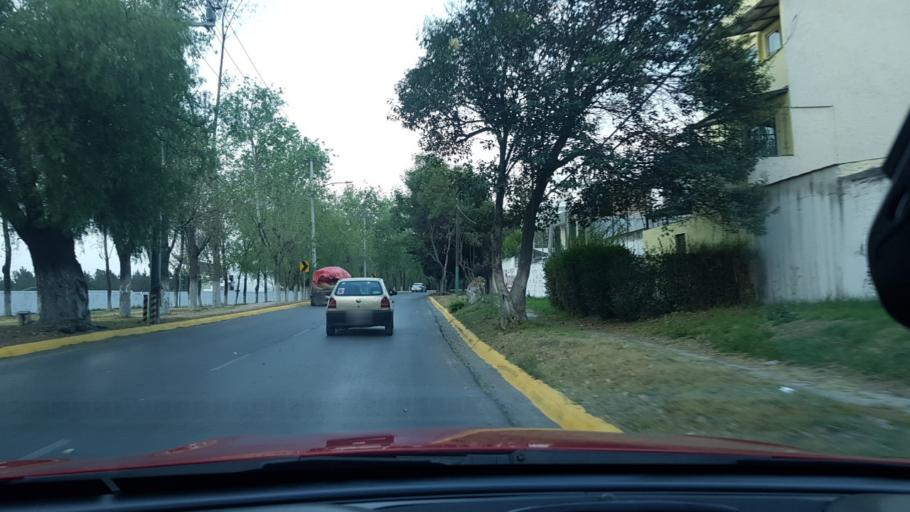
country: MX
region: Mexico
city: Cuautitlan Izcalli
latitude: 19.6462
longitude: -99.2254
